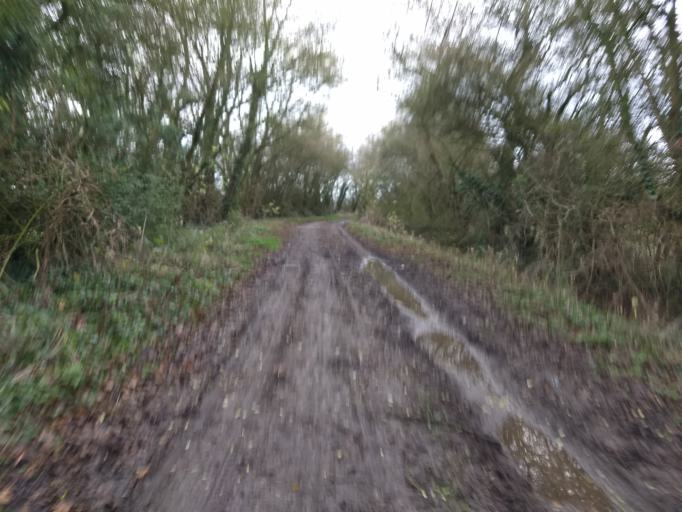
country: GB
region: England
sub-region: Buckinghamshire
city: Newton Longville
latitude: 51.9856
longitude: -0.7863
